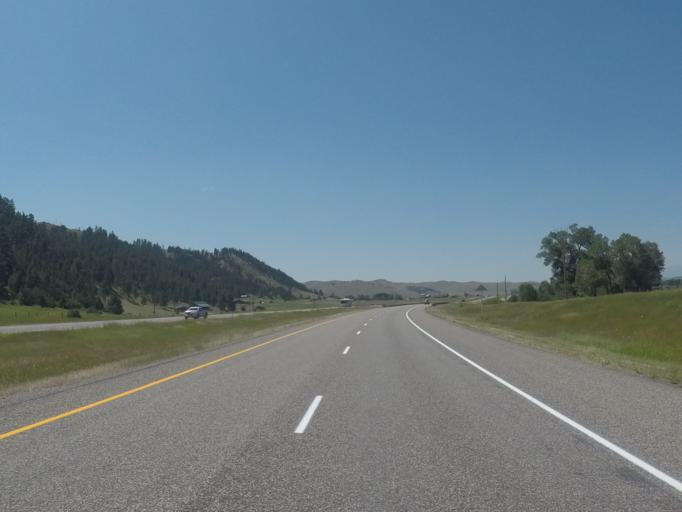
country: US
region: Montana
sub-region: Stillwater County
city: Absarokee
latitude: 45.7066
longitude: -109.6040
